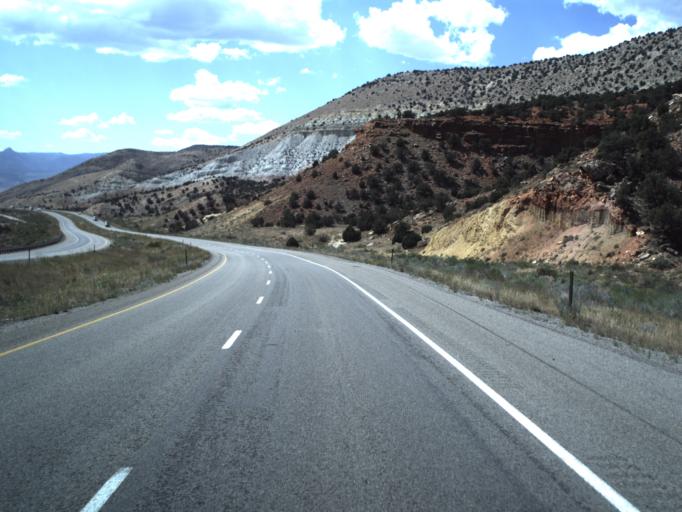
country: US
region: Utah
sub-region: Sevier County
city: Salina
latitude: 38.9324
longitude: -111.7900
